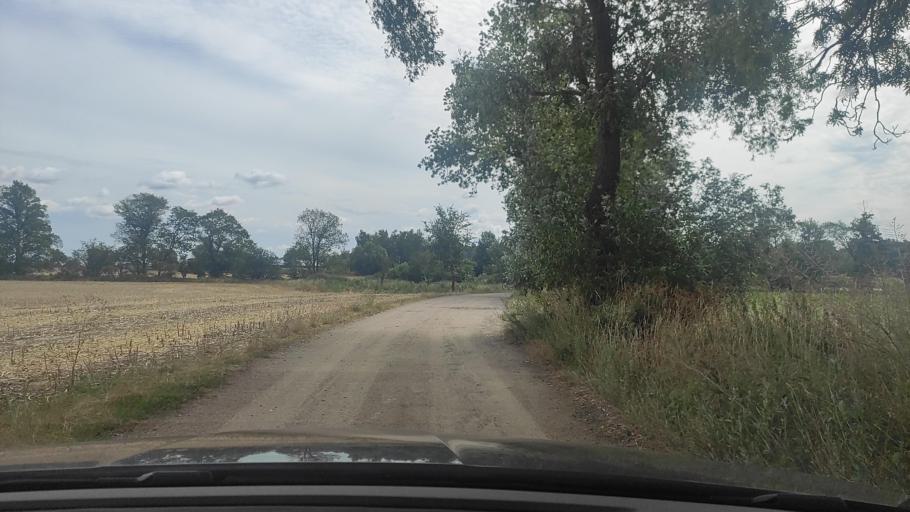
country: PL
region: Greater Poland Voivodeship
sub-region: Powiat poznanski
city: Kostrzyn
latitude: 52.4105
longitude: 17.1776
